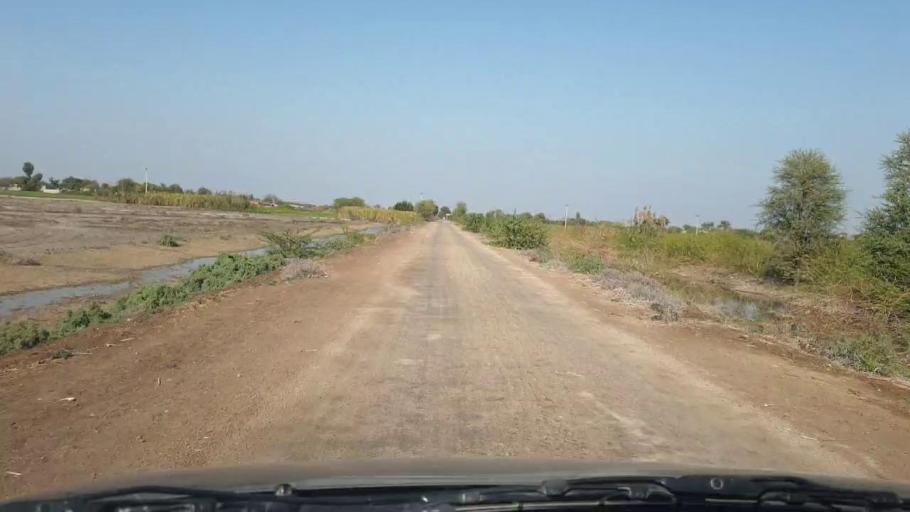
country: PK
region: Sindh
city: Samaro
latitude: 25.1682
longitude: 69.2844
